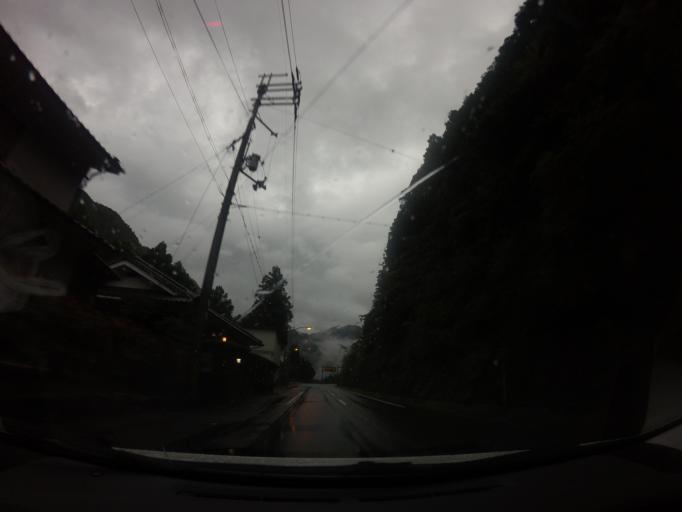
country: JP
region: Wakayama
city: Koya
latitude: 34.0060
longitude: 135.7934
